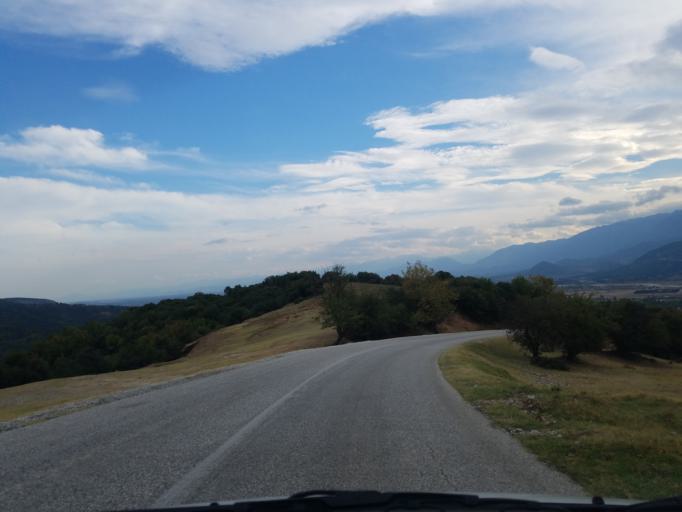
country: GR
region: Thessaly
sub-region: Trikala
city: Kalampaka
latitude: 39.7114
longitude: 21.6532
